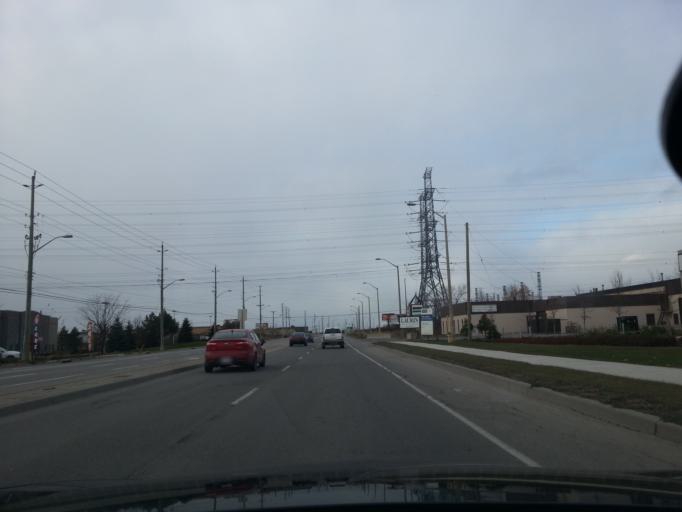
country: CA
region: Ontario
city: Ottawa
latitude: 45.3860
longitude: -75.6039
